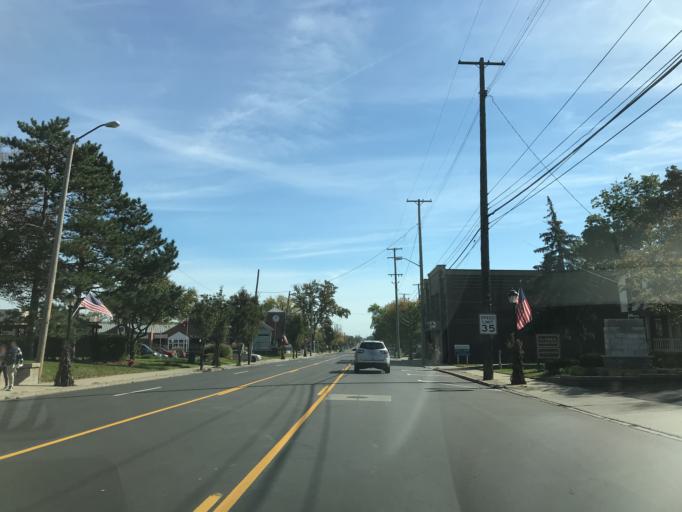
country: US
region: Michigan
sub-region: Oakland County
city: Farmington
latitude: 42.4632
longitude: -83.3724
